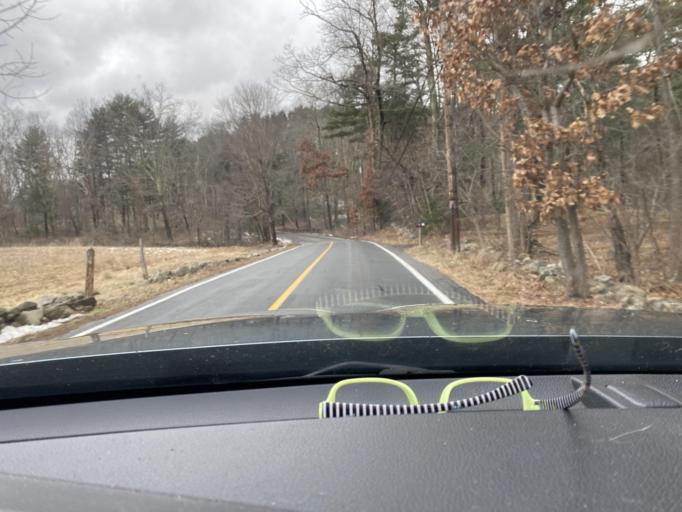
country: US
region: Massachusetts
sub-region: Middlesex County
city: Sherborn
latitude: 42.2120
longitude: -71.3832
